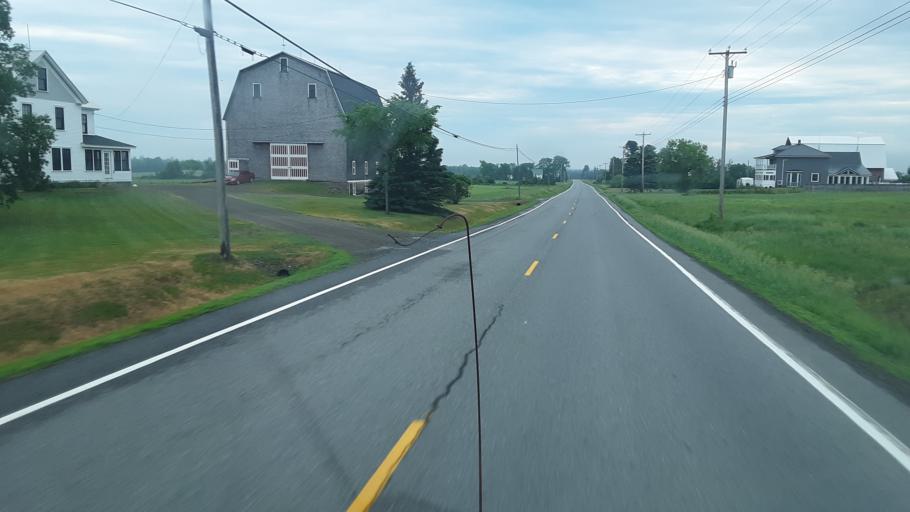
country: US
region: Maine
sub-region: Aroostook County
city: Presque Isle
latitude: 46.6037
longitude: -68.3936
